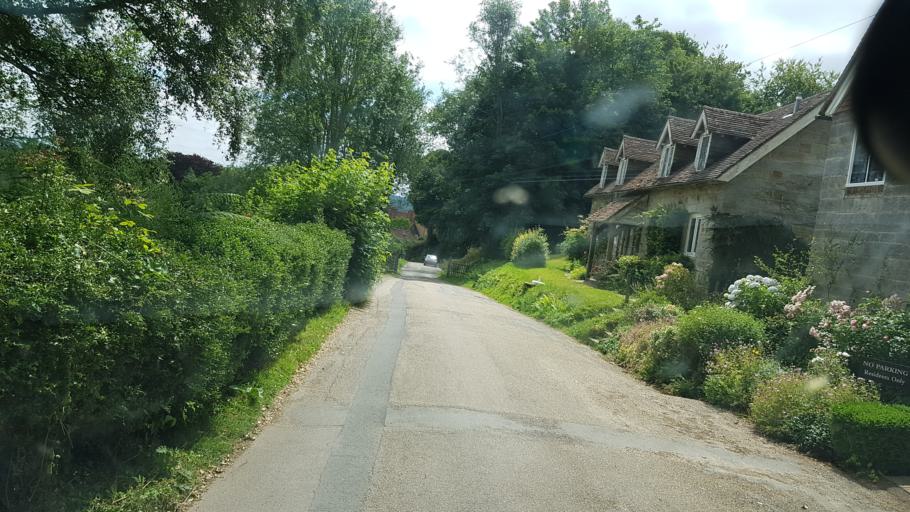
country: GB
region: England
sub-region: West Sussex
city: East Grinstead
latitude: 51.1047
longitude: -0.0188
